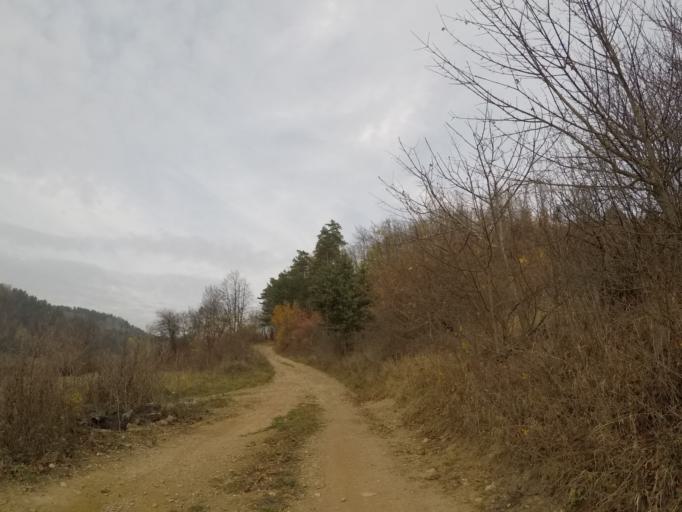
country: SK
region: Presovsky
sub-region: Okres Presov
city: Presov
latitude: 48.9199
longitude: 21.1433
